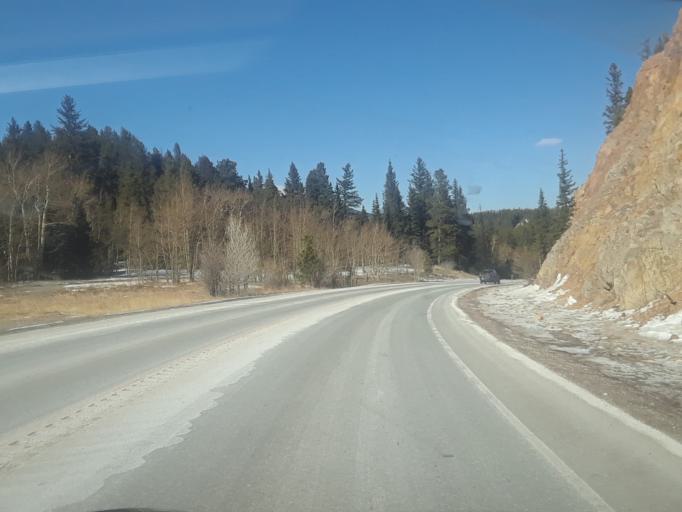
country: US
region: Colorado
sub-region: Boulder County
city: Nederland
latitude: 40.1025
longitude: -105.4877
